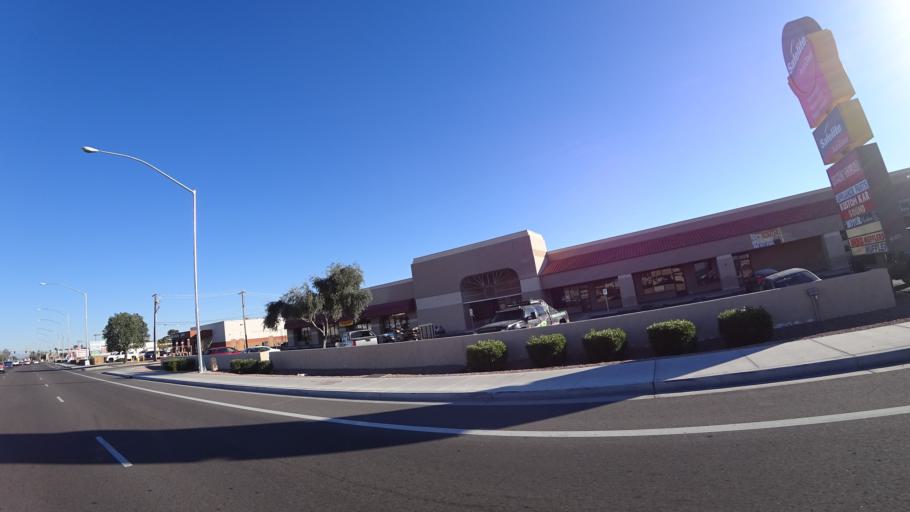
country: US
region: Arizona
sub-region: Maricopa County
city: Mesa
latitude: 33.3933
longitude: -111.8258
